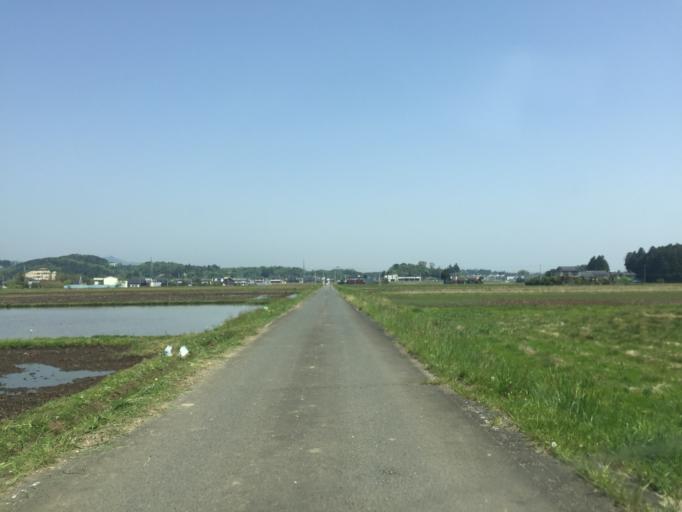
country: JP
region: Miyagi
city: Marumori
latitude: 37.7782
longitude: 140.9108
